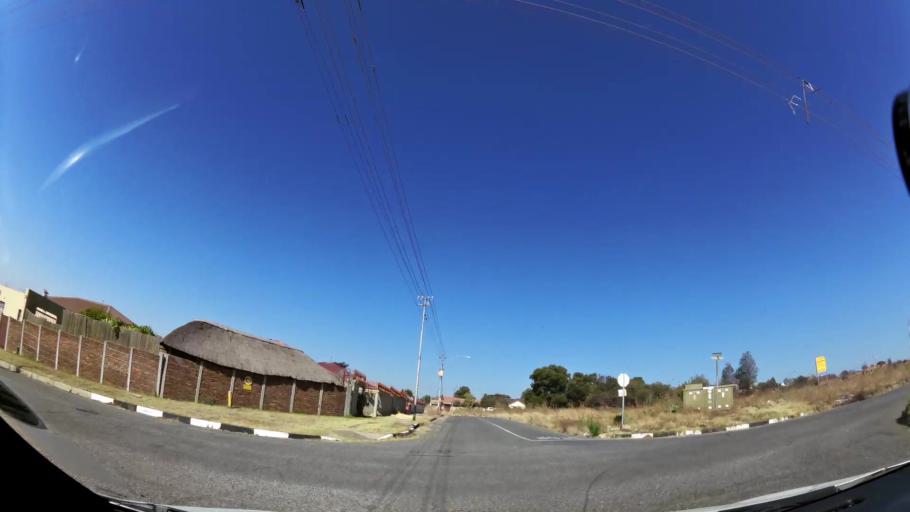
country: ZA
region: Gauteng
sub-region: City of Johannesburg Metropolitan Municipality
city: Johannesburg
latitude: -26.2555
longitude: 28.0874
